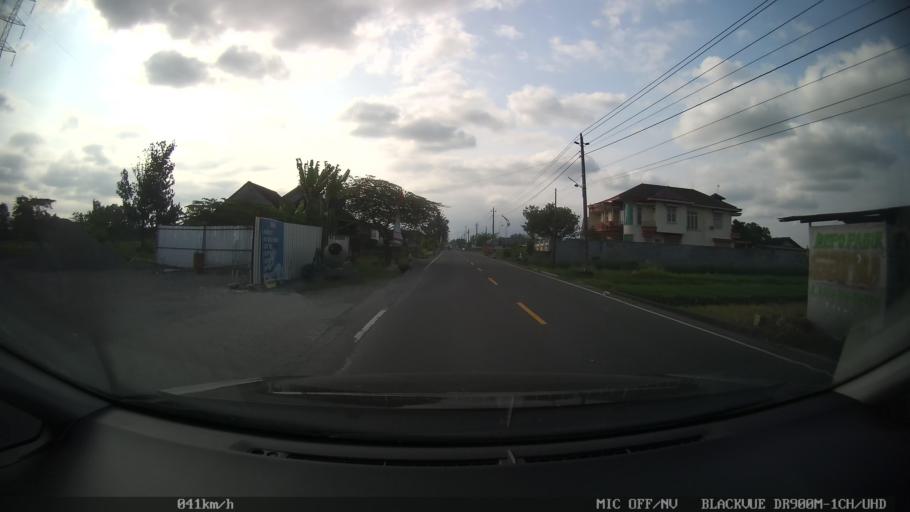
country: ID
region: Central Java
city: Candi Prambanan
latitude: -7.7136
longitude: 110.4710
